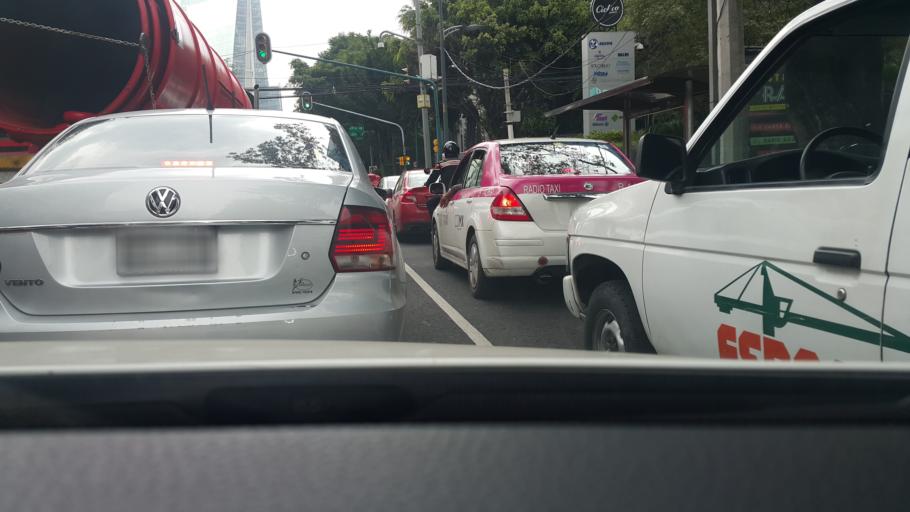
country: MX
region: Mexico City
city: Alvaro Obregon
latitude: 19.3640
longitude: -99.1821
